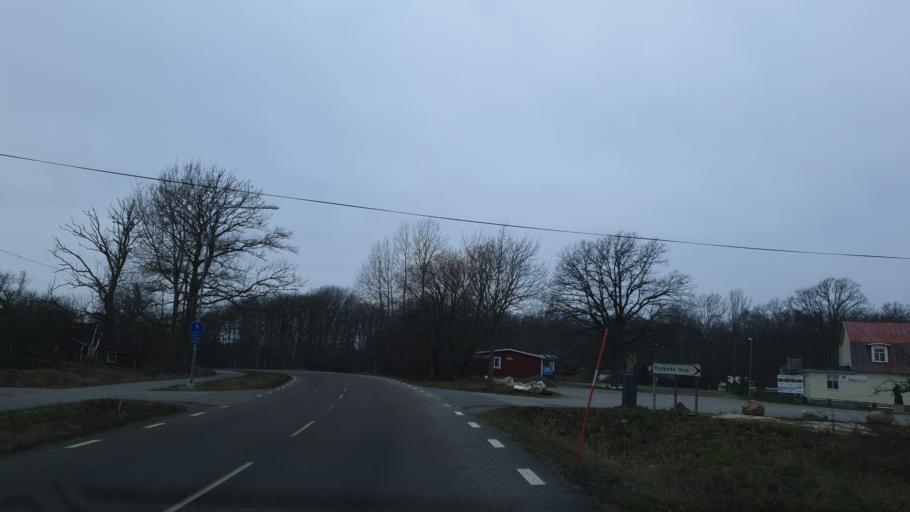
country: SE
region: Blekinge
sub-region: Karlskrona Kommun
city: Sturko
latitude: 56.1153
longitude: 15.6694
